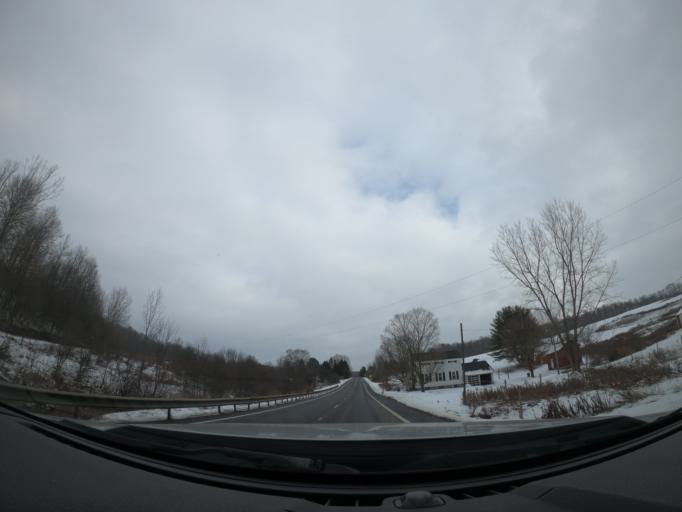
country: US
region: New York
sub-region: Cortland County
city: Cortland West
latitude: 42.6734
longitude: -76.2728
